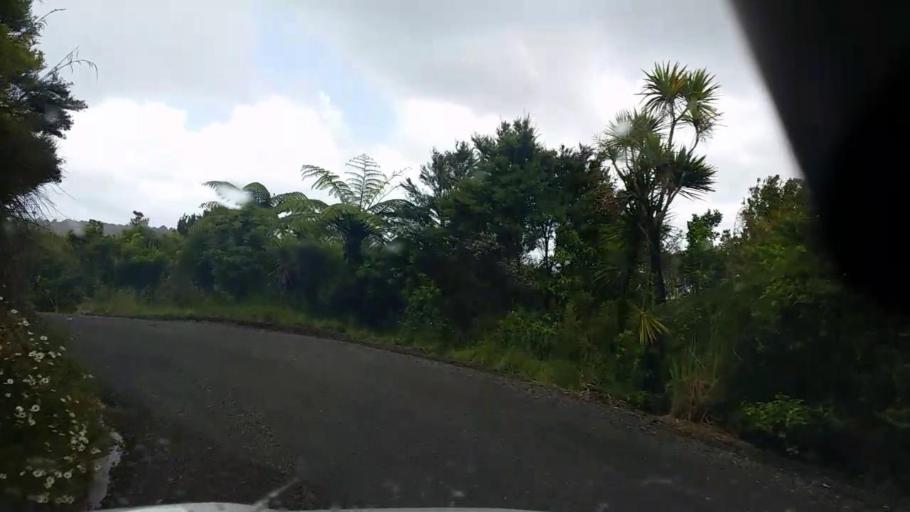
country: NZ
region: Auckland
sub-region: Auckland
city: Muriwai Beach
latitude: -36.9365
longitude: 174.5110
